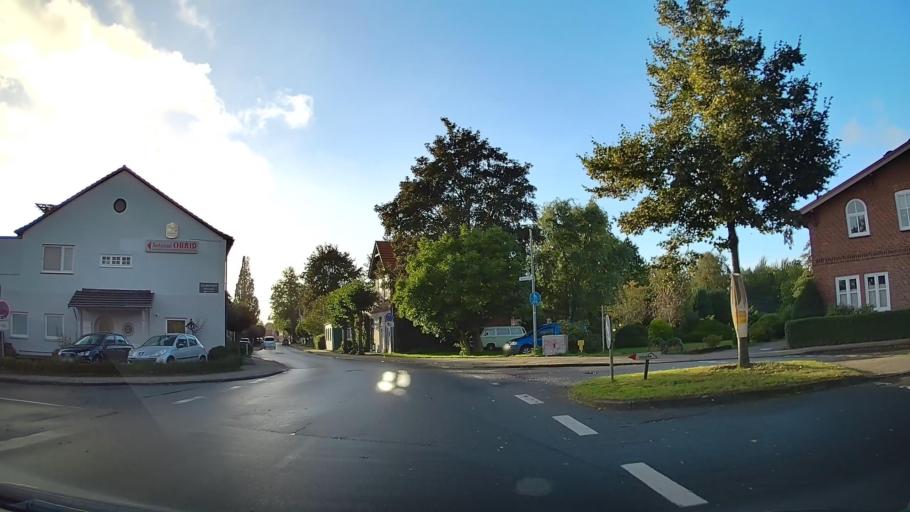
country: DE
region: Schleswig-Holstein
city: Horst
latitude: 53.8124
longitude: 9.6256
